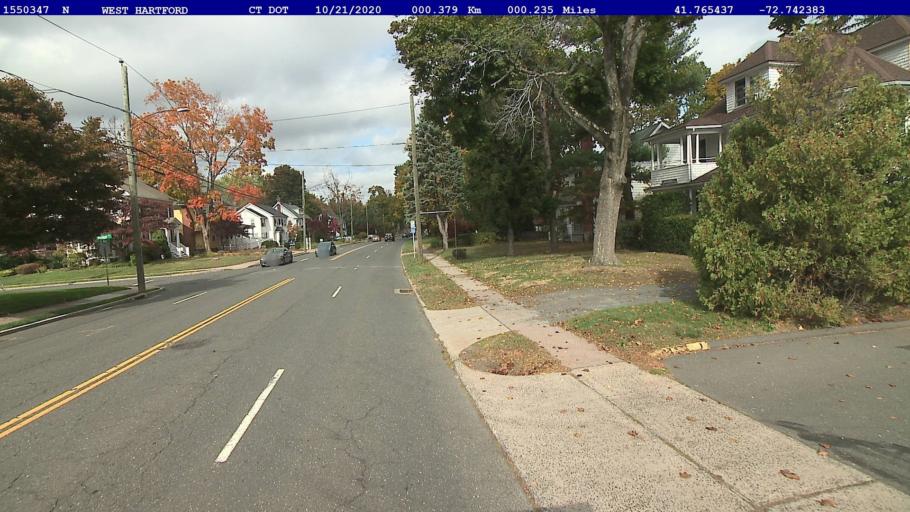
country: US
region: Connecticut
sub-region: Hartford County
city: West Hartford
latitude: 41.7654
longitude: -72.7424
